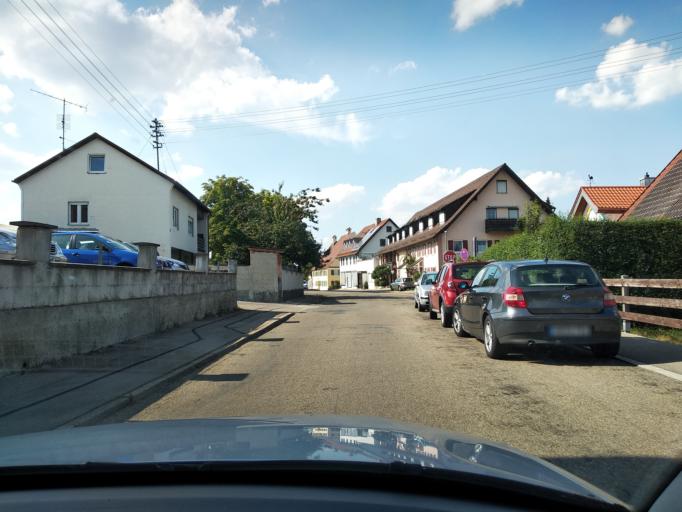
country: DE
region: Bavaria
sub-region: Swabia
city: Memmingen
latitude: 48.0031
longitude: 10.1818
